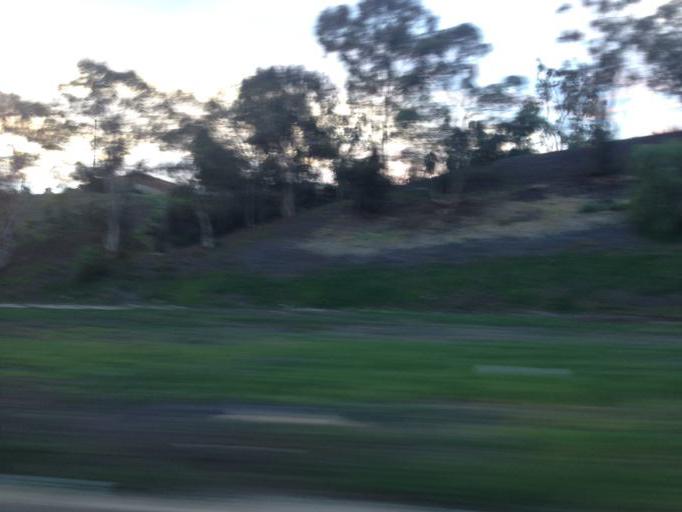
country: US
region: California
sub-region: San Diego County
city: San Diego
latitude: 32.7388
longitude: -117.1153
